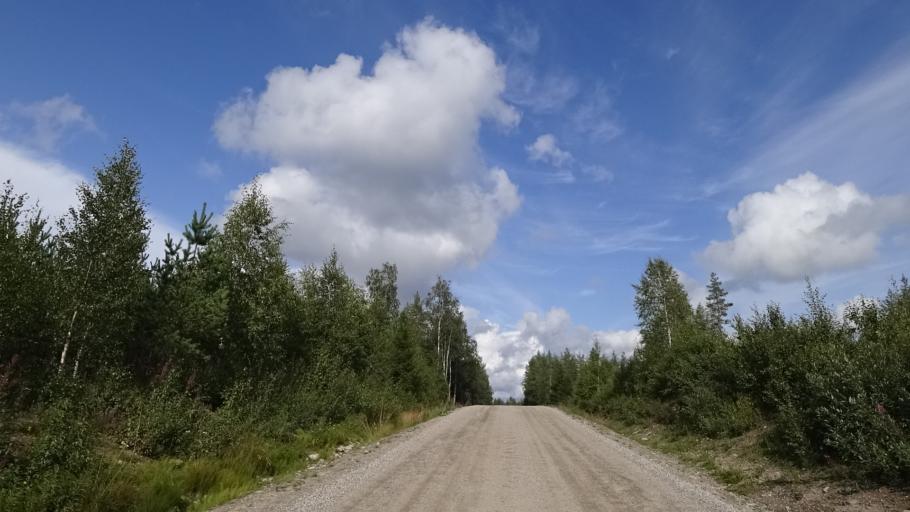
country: FI
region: North Karelia
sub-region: Pielisen Karjala
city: Lieksa
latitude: 63.5801
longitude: 30.1283
